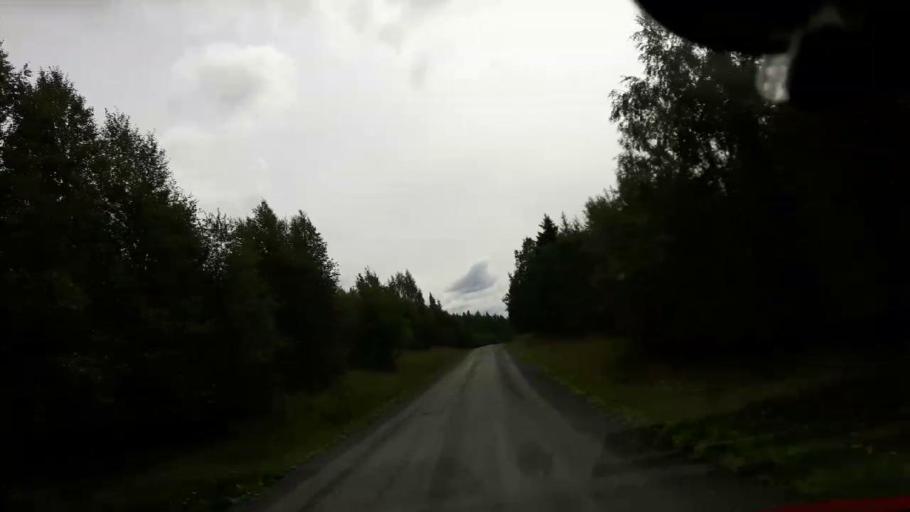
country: SE
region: Jaemtland
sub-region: Krokoms Kommun
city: Valla
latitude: 63.6655
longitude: 13.9659
